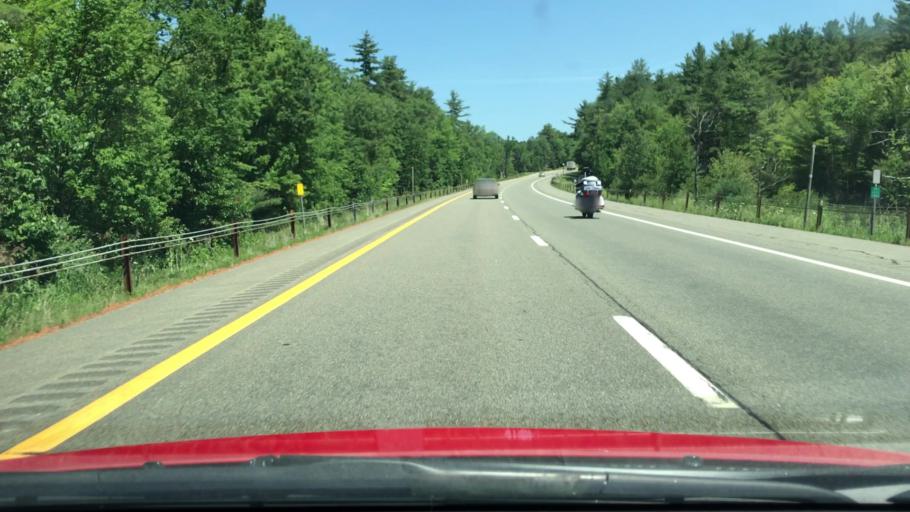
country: US
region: New York
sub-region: Essex County
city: Keeseville
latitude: 44.3735
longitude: -73.5247
